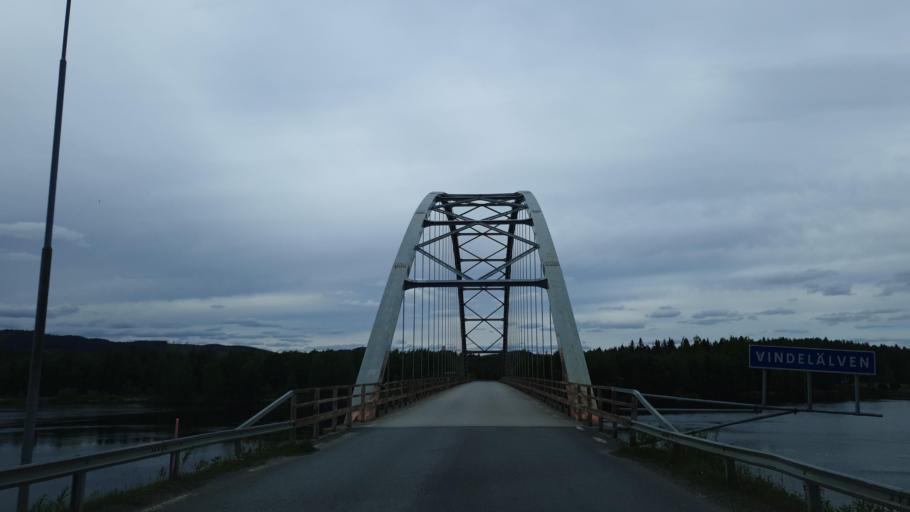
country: SE
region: Vaesterbotten
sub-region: Sorsele Kommun
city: Sorsele
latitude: 65.5421
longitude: 17.5115
